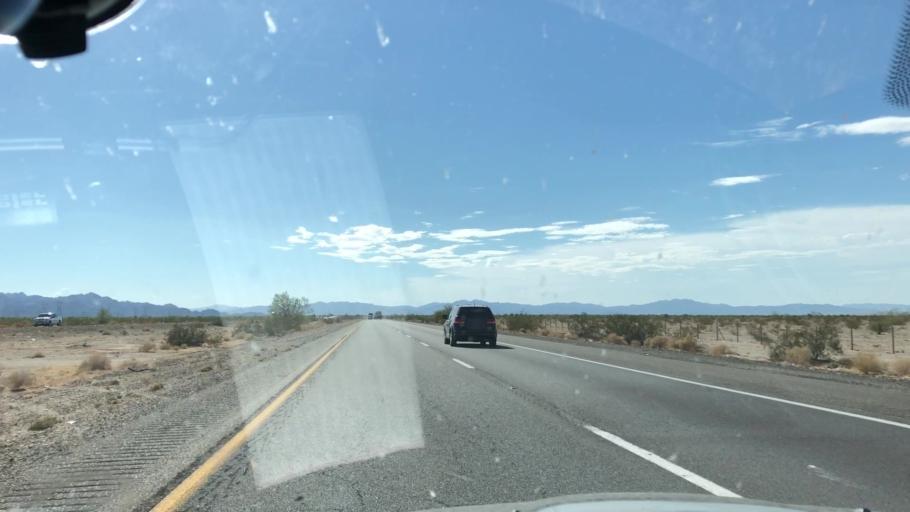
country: US
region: California
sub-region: Riverside County
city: Mesa Verde
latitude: 33.6673
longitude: -115.1917
